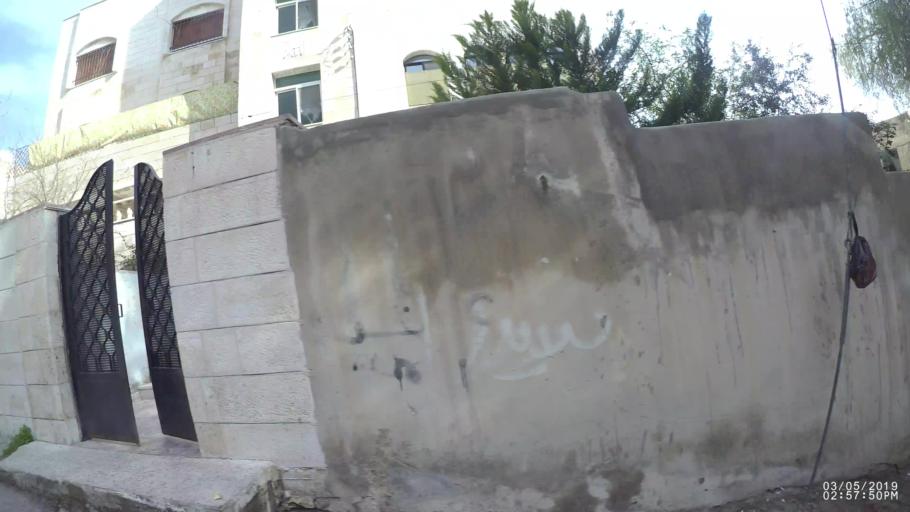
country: JO
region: Amman
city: Amman
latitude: 31.9986
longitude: 35.9456
